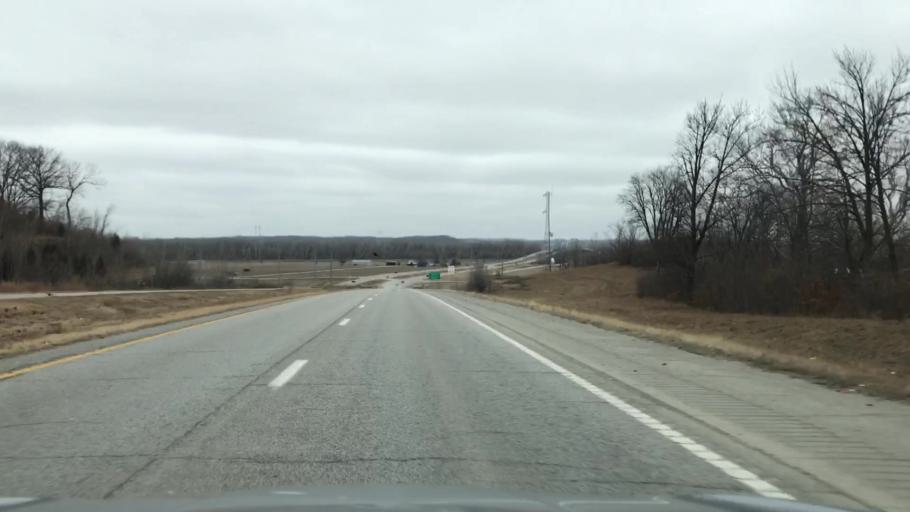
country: US
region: Missouri
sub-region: Jackson County
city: Independence
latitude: 39.1531
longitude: -94.3935
